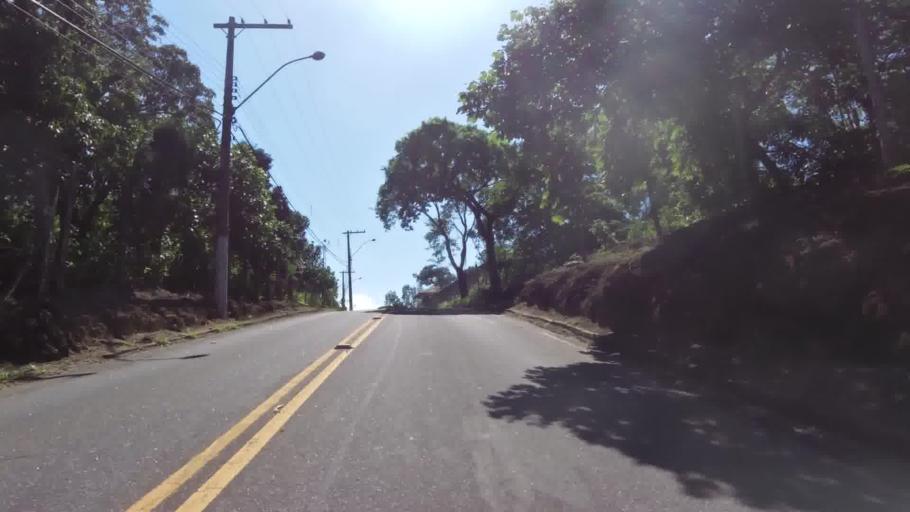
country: BR
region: Espirito Santo
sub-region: Piuma
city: Piuma
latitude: -20.8236
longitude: -40.6286
